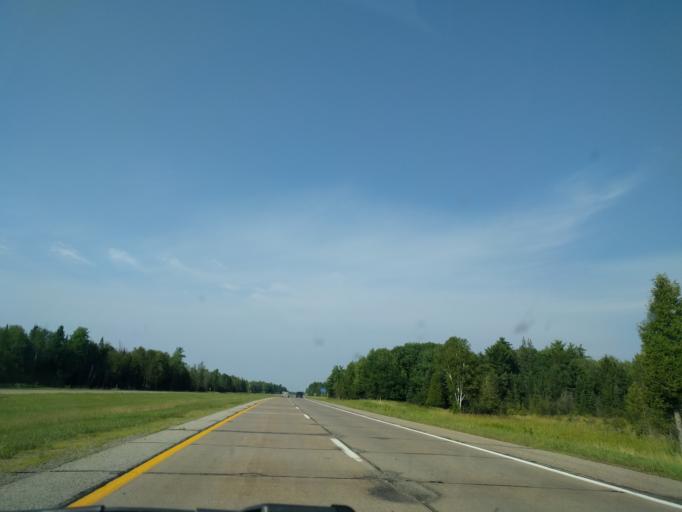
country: US
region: Michigan
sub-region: Delta County
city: Gladstone
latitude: 45.8859
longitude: -87.0081
